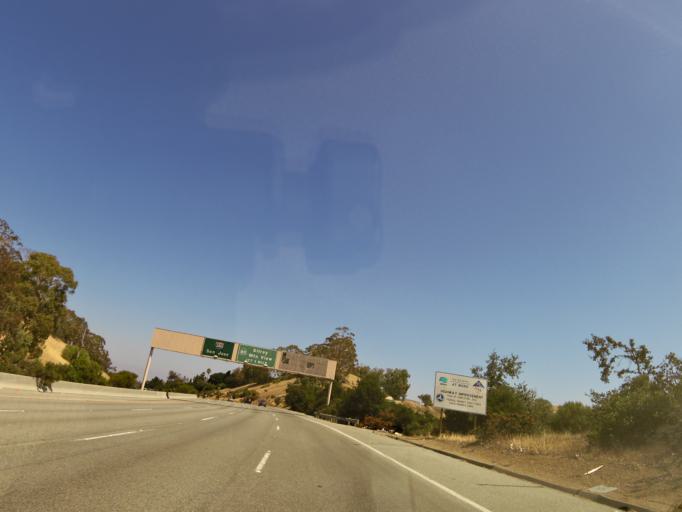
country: US
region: California
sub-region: Santa Clara County
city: Loyola
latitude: 37.3337
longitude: -122.0780
